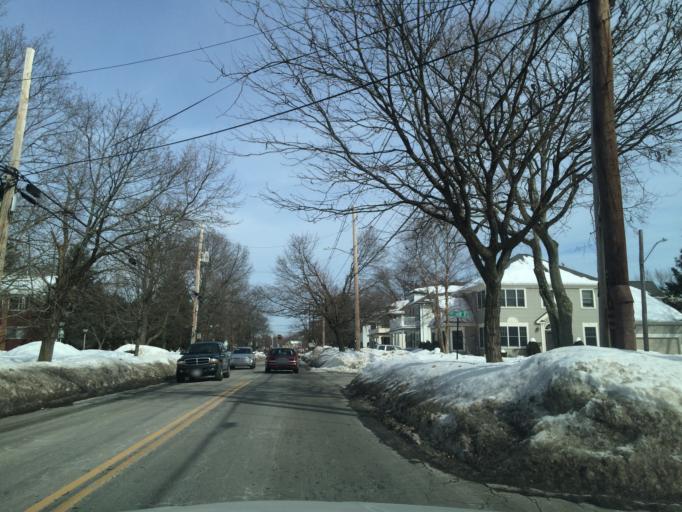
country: US
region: Massachusetts
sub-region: Middlesex County
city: Newton
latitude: 42.3552
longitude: -71.2109
